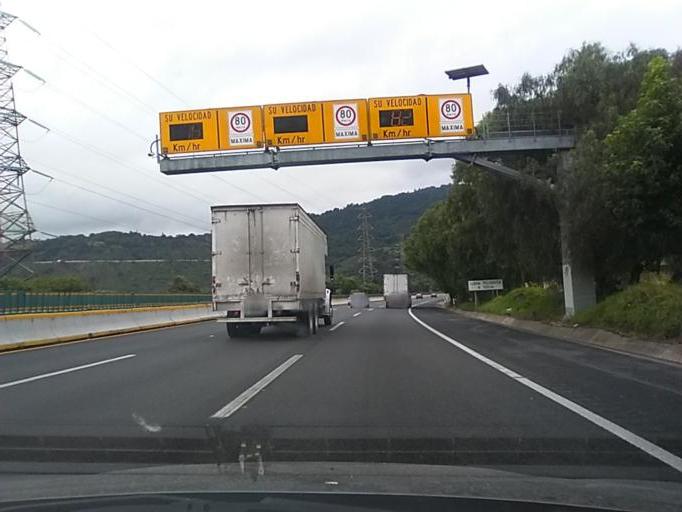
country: MX
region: Mexico City
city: Xochimilco
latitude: 19.2338
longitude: -99.1443
